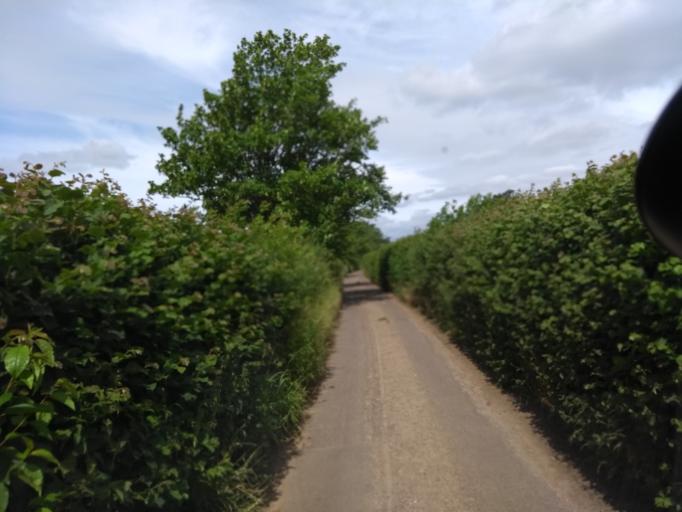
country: GB
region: England
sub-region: Somerset
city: Ilminster
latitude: 50.9245
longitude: -2.8653
